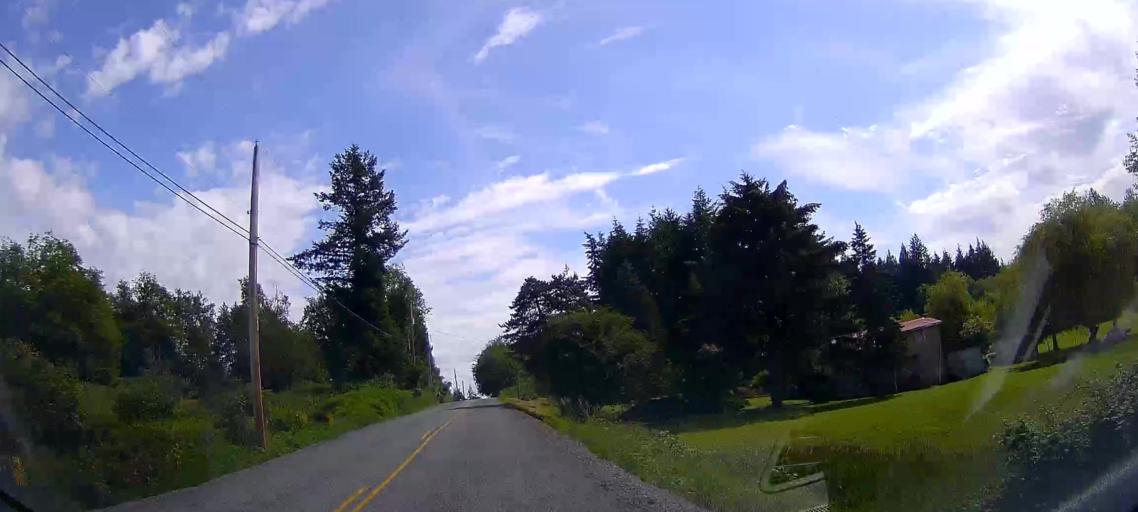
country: US
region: Washington
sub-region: Skagit County
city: Burlington
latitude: 48.5634
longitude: -122.3618
